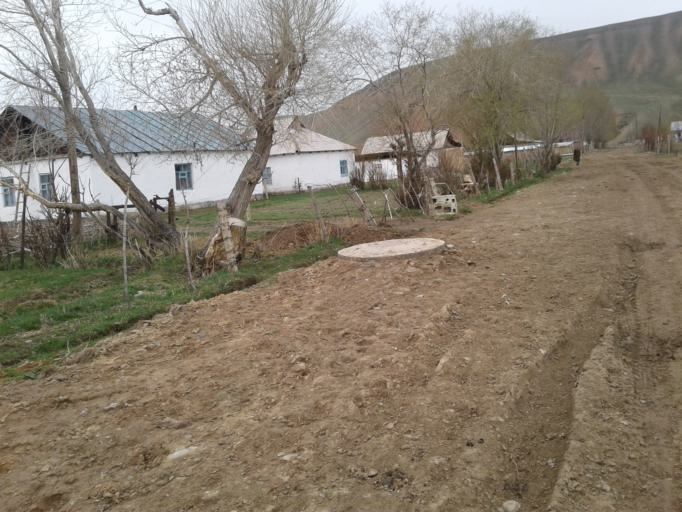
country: KG
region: Naryn
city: Naryn
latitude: 41.5148
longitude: 76.4368
